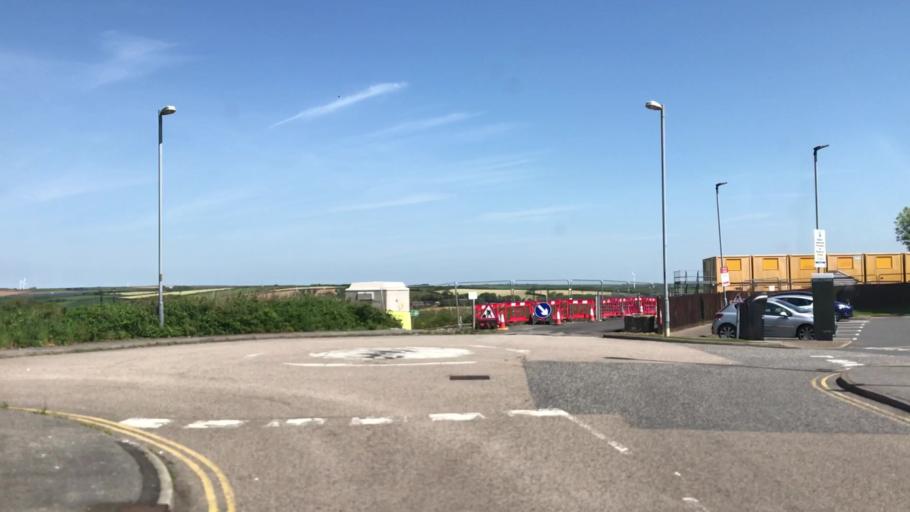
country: GB
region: England
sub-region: Cornwall
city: Truro
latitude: 50.2647
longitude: -5.1030
